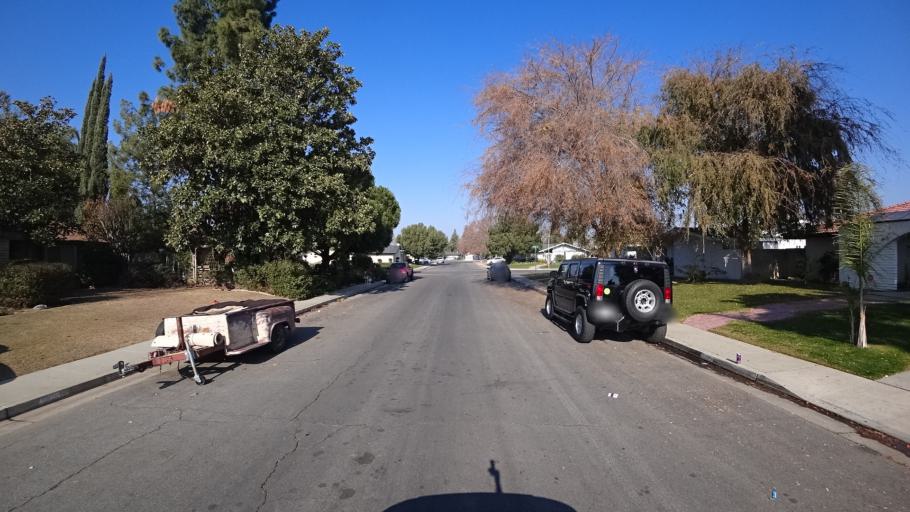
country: US
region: California
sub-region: Kern County
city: Greenacres
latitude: 35.3568
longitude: -119.0731
